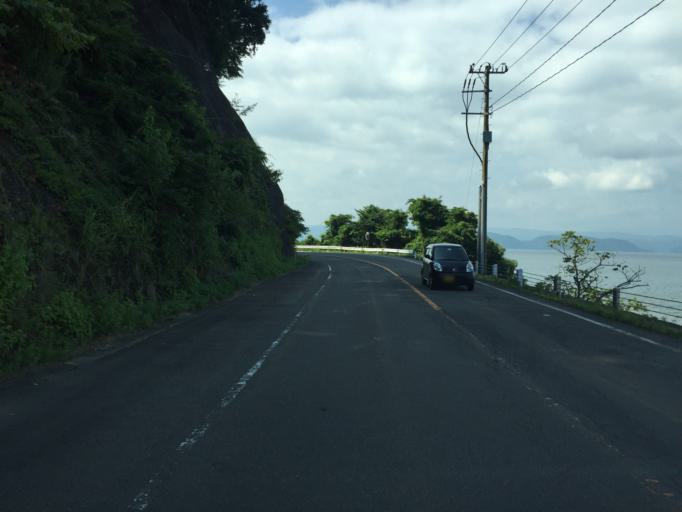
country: JP
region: Fukushima
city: Inawashiro
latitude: 37.4565
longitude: 140.1519
